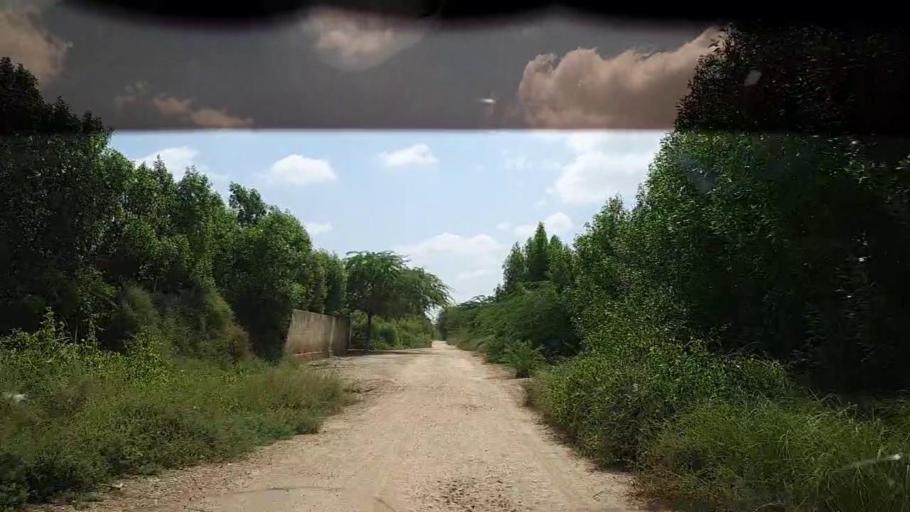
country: PK
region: Sindh
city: Kadhan
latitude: 24.5891
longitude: 68.9582
